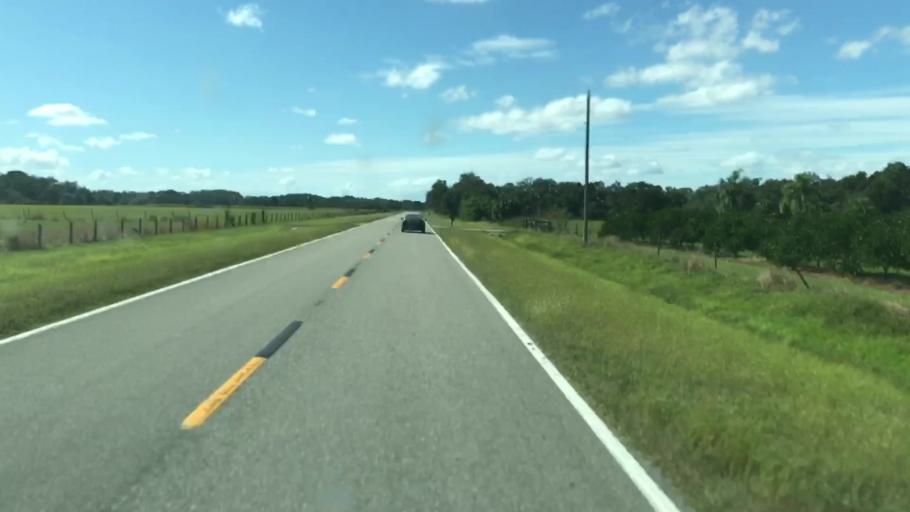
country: US
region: Florida
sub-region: Lee County
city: Fort Myers Shores
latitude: 26.7401
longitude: -81.7403
